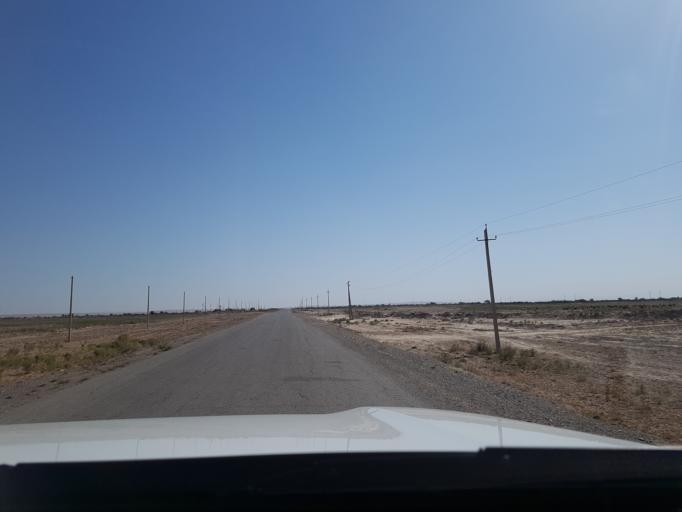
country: IR
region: Razavi Khorasan
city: Sarakhs
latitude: 36.5023
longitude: 61.2536
